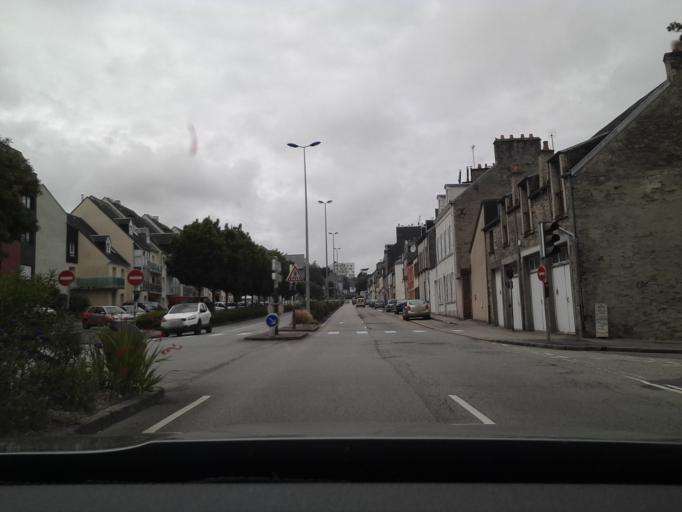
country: FR
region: Lower Normandy
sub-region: Departement de la Manche
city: Cherbourg-Octeville
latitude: 49.6347
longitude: -1.6266
